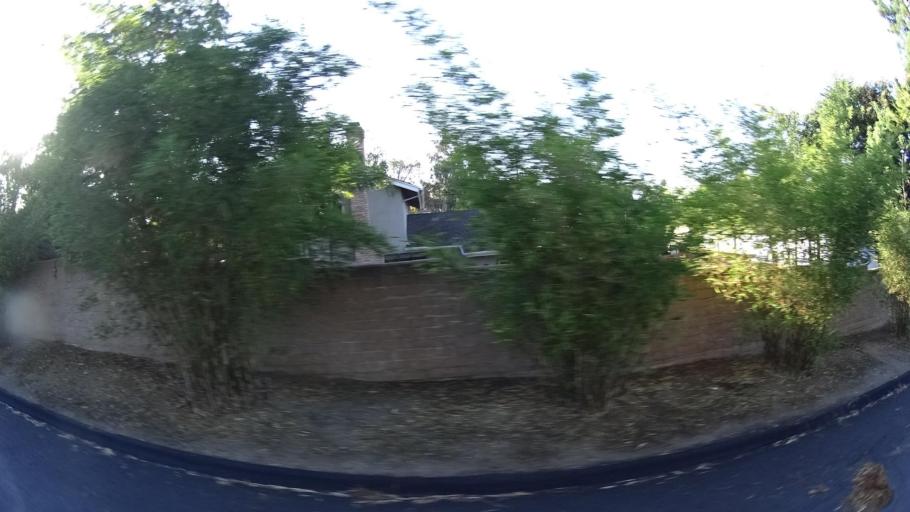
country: US
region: California
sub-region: San Diego County
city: Casa de Oro-Mount Helix
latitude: 32.7637
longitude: -116.9893
